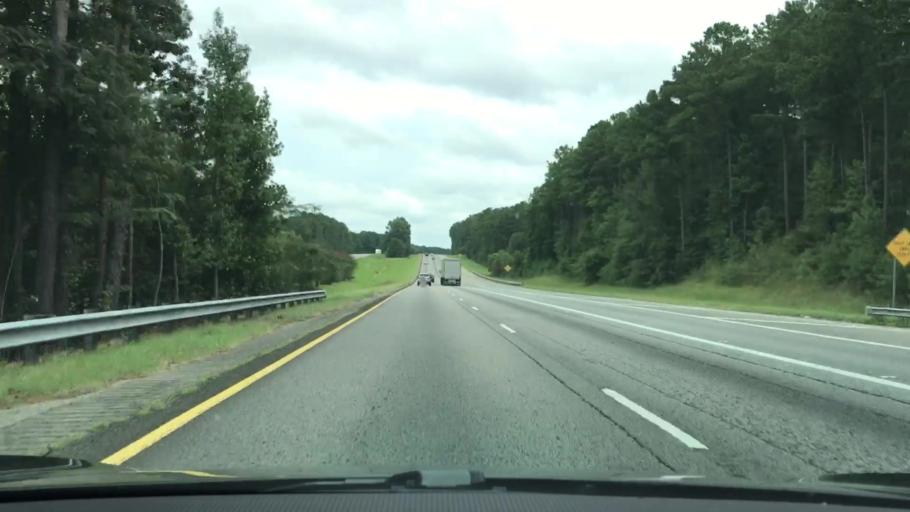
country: US
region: Georgia
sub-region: Troup County
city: West Point
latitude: 32.9392
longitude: -85.1029
